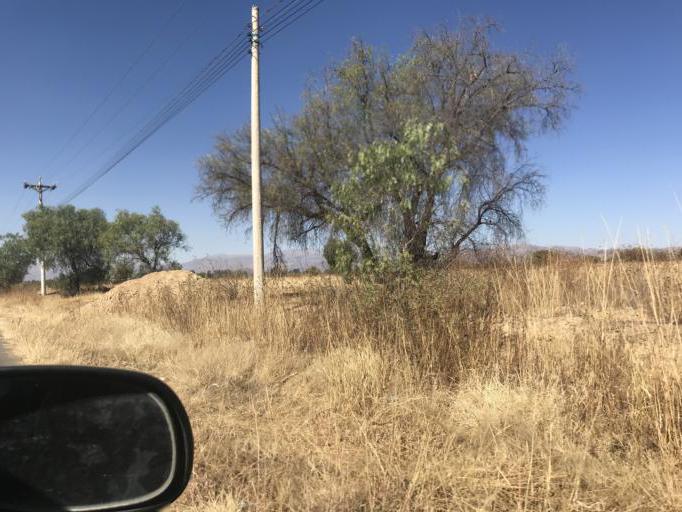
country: BO
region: Cochabamba
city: Cliza
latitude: -17.6002
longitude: -65.9675
